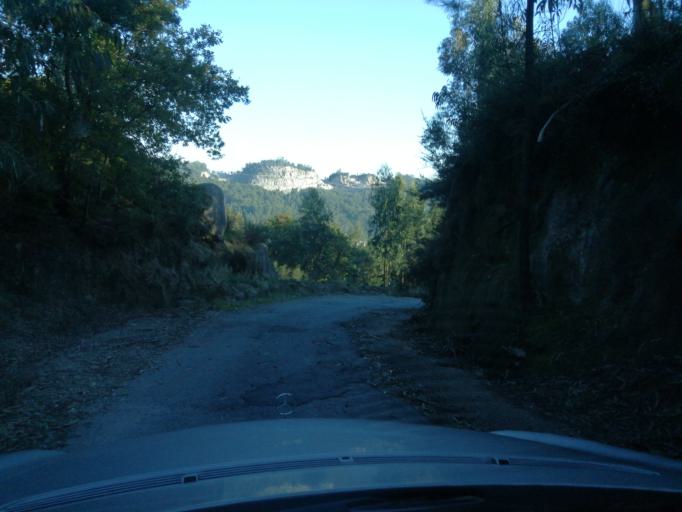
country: PT
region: Braga
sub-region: Braga
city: Oliveira
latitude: 41.4656
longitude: -8.4496
